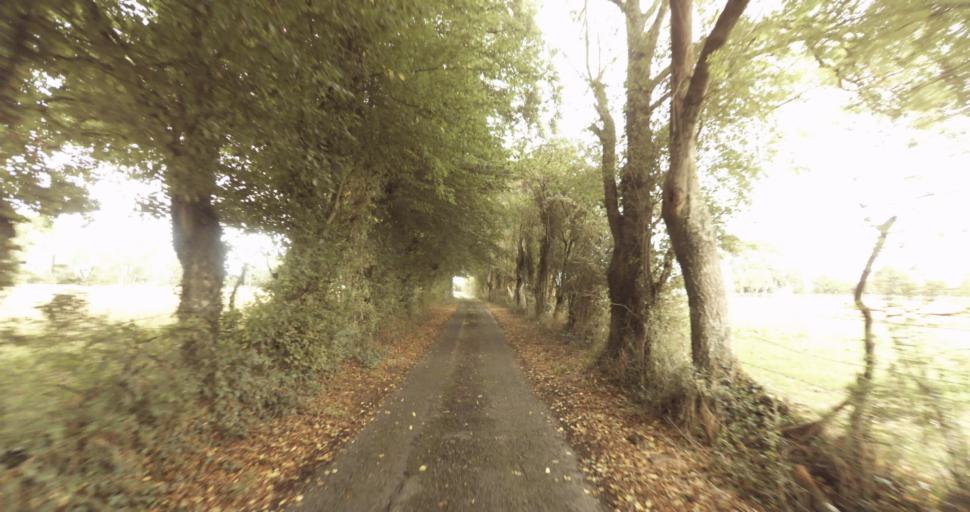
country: FR
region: Lower Normandy
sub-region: Departement de l'Orne
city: Sainte-Gauburge-Sainte-Colombe
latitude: 48.7323
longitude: 0.4803
